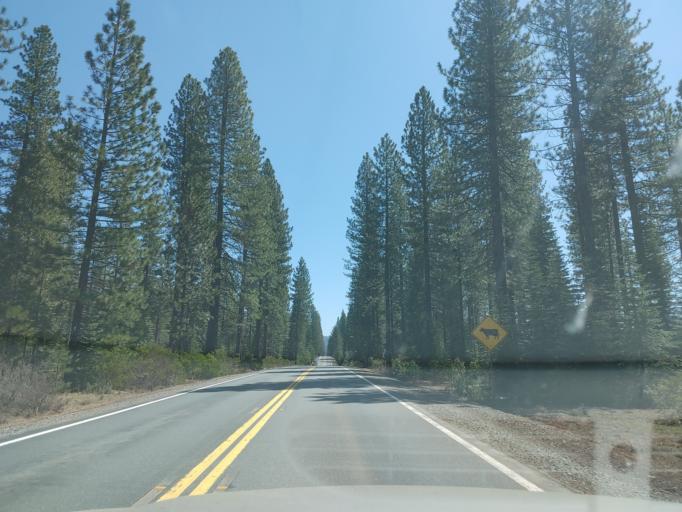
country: US
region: California
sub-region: Siskiyou County
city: McCloud
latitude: 41.2594
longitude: -121.8402
